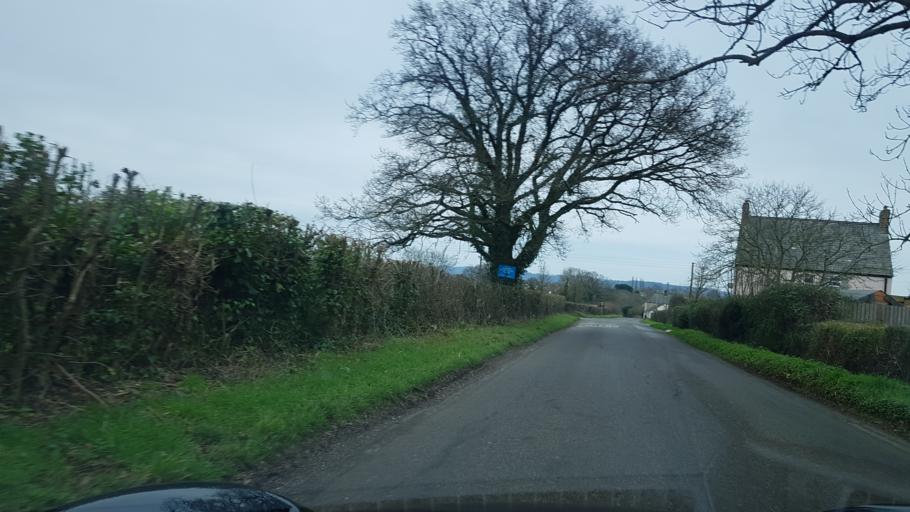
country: GB
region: England
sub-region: Somerset
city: Chard
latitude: 50.9336
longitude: -2.9777
